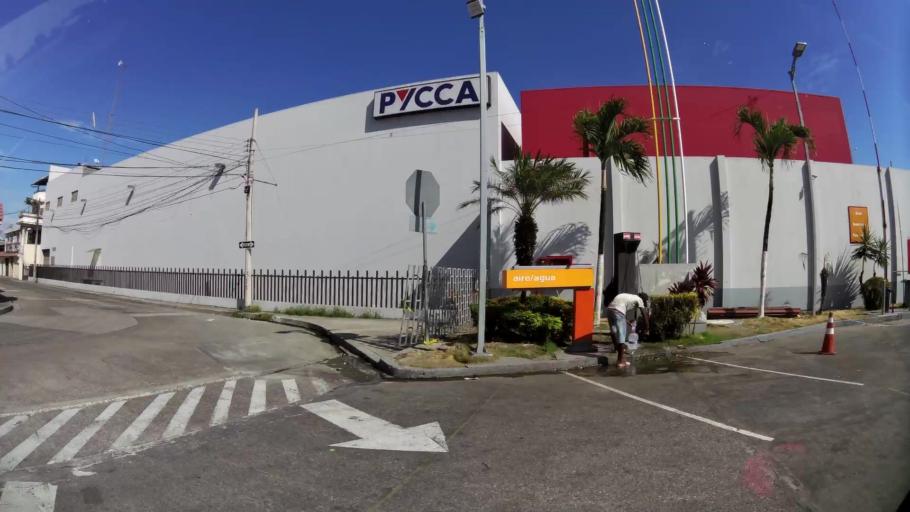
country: EC
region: Guayas
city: Guayaquil
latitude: -2.2298
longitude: -79.8970
